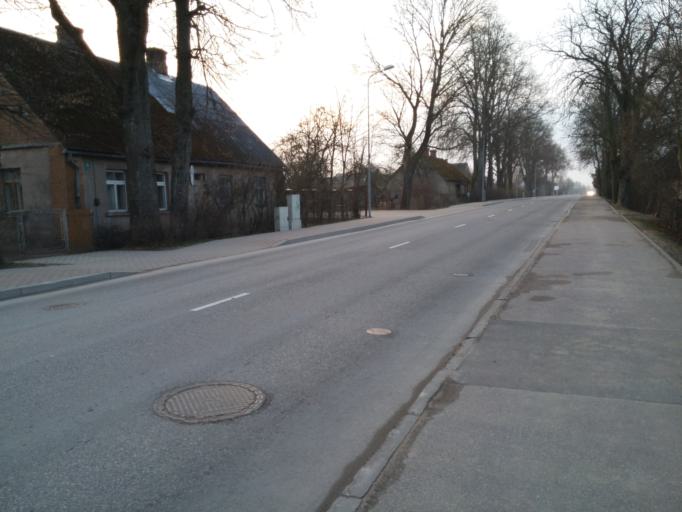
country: LV
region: Dobeles Rajons
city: Dobele
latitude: 56.6162
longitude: 23.2867
